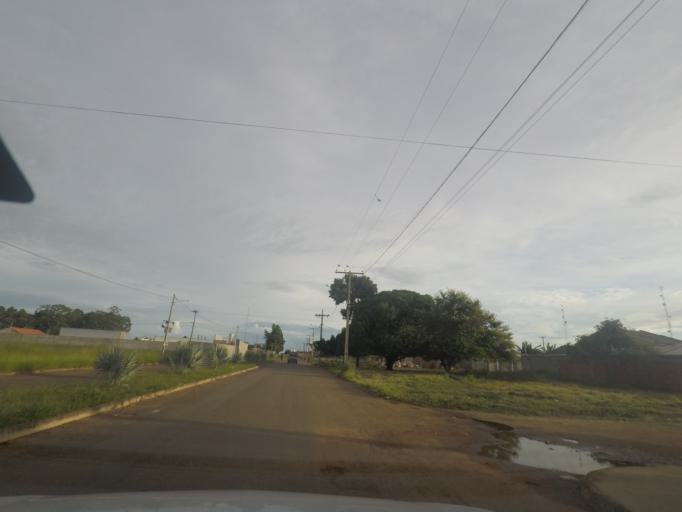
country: BR
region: Goias
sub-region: Trindade
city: Trindade
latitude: -16.7228
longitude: -49.4396
